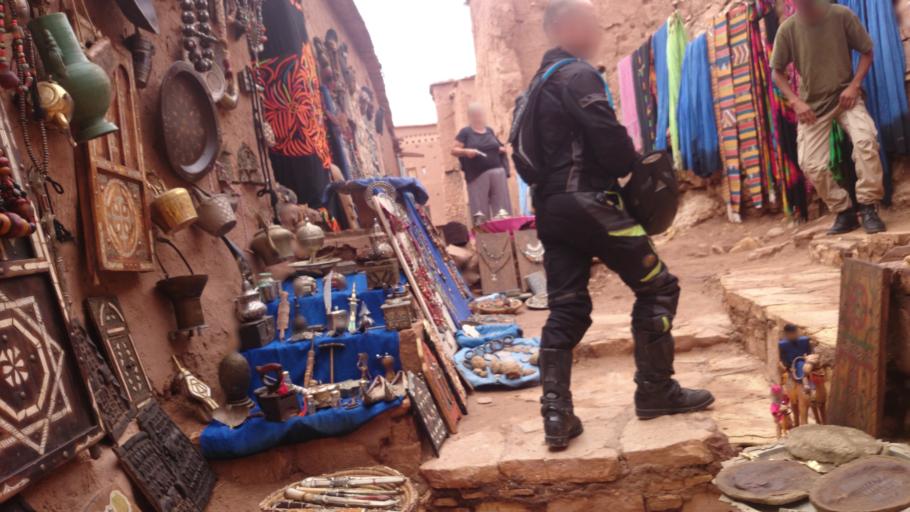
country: MA
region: Souss-Massa-Draa
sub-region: Ouarzazate
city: Amerzgane
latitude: 31.0471
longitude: -7.1289
